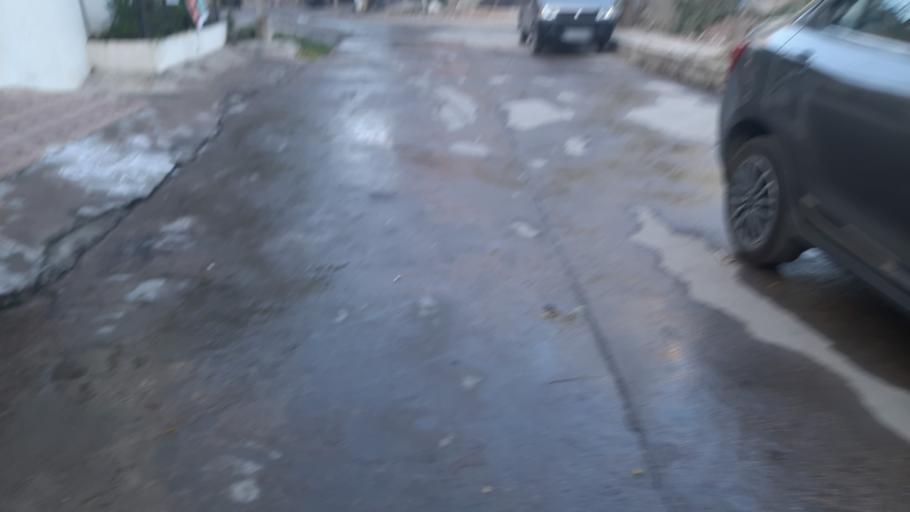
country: IN
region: Telangana
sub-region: Rangareddi
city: Gaddi Annaram
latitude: 17.3439
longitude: 78.5266
